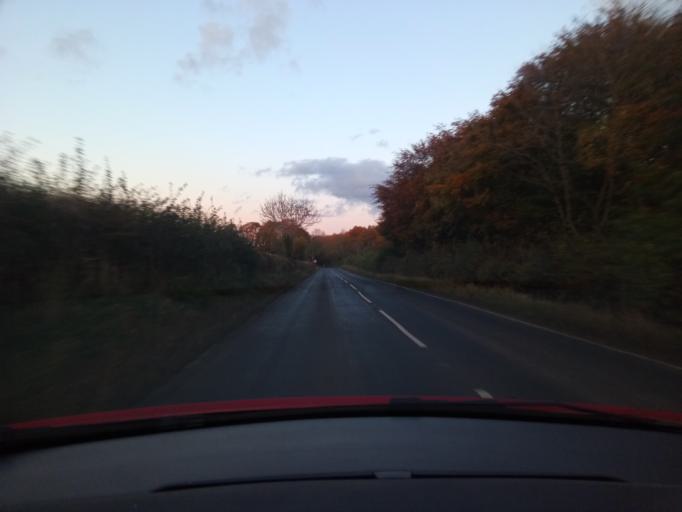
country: GB
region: England
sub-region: Northumberland
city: Bardon Mill
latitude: 54.9604
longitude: -2.2512
